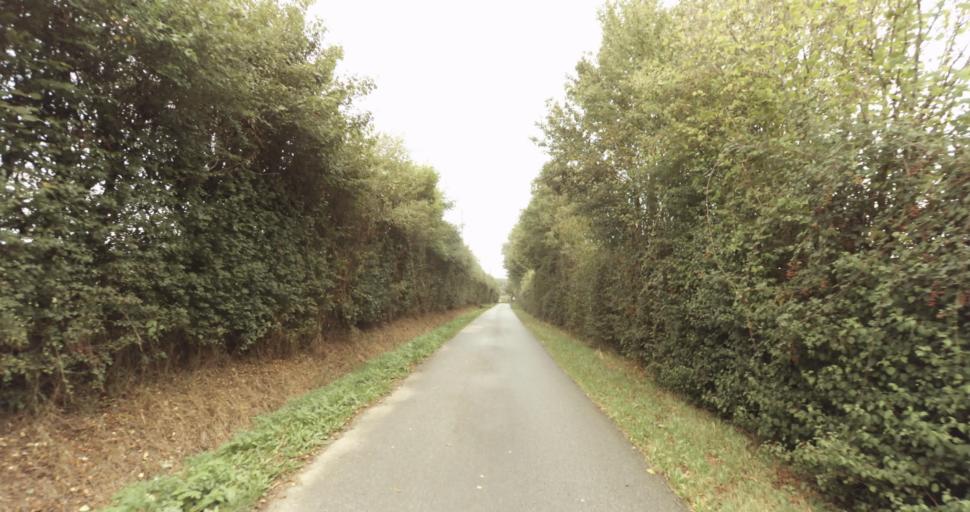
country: FR
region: Lower Normandy
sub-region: Departement de l'Orne
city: Sainte-Gauburge-Sainte-Colombe
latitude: 48.7431
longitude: 0.4527
